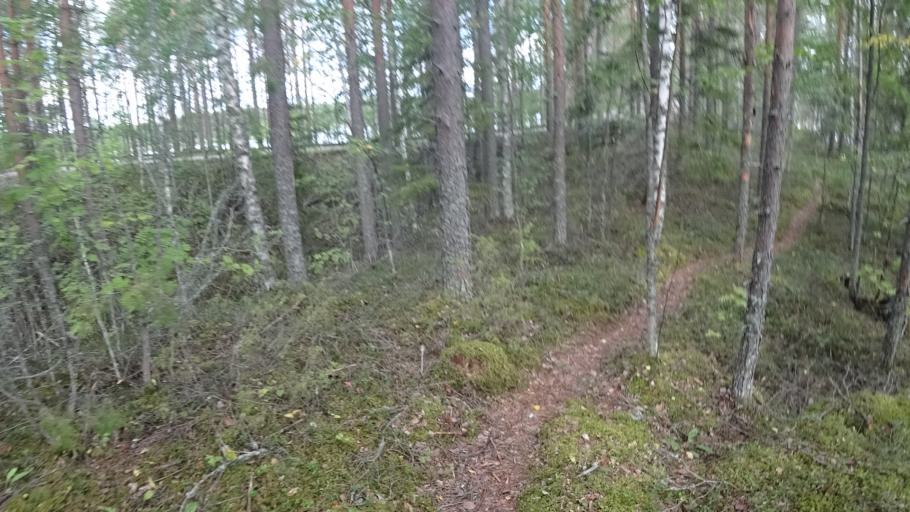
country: FI
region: North Karelia
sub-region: Joensuu
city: Ilomantsi
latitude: 62.6136
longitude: 31.1959
